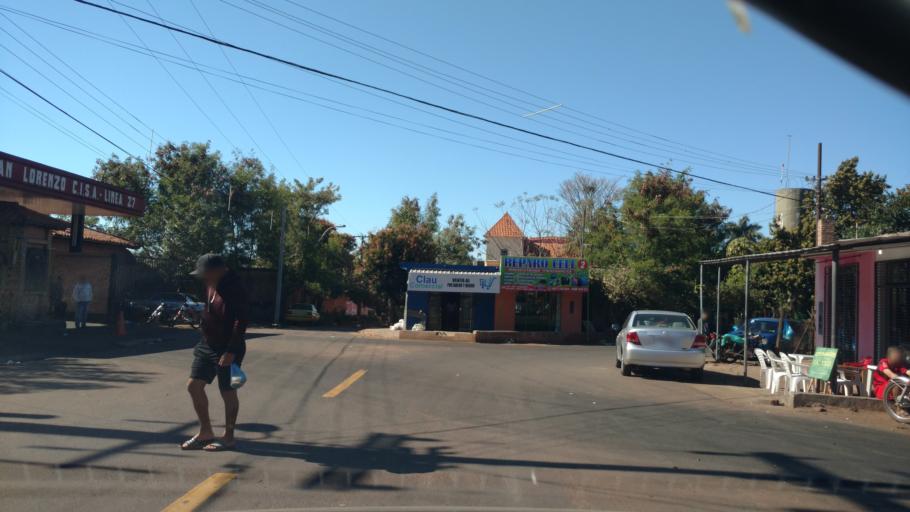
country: PY
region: Central
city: Capiata
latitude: -25.3742
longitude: -57.4077
